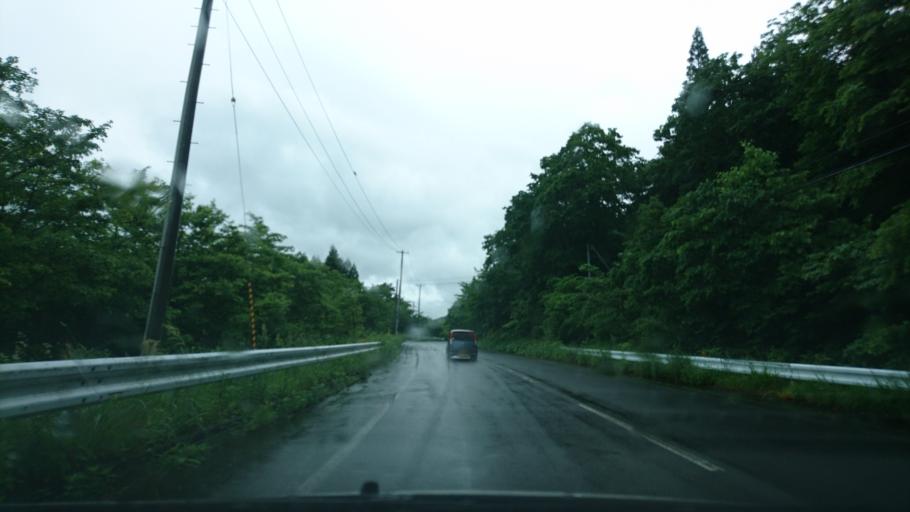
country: JP
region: Iwate
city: Ichinoseki
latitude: 39.0041
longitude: 140.8965
